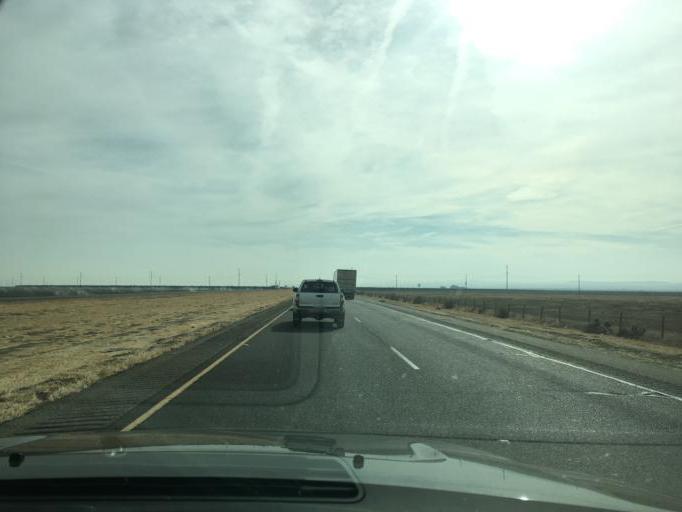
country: US
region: California
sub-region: Fresno County
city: Huron
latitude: 36.1575
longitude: -120.1771
